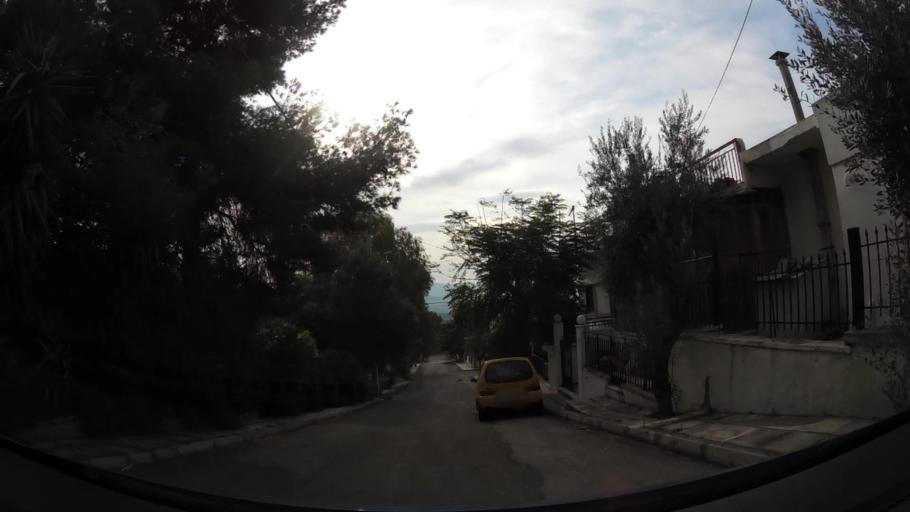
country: GR
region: Attica
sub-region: Nomarchia Athinas
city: Kamateron
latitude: 38.0561
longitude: 23.7018
